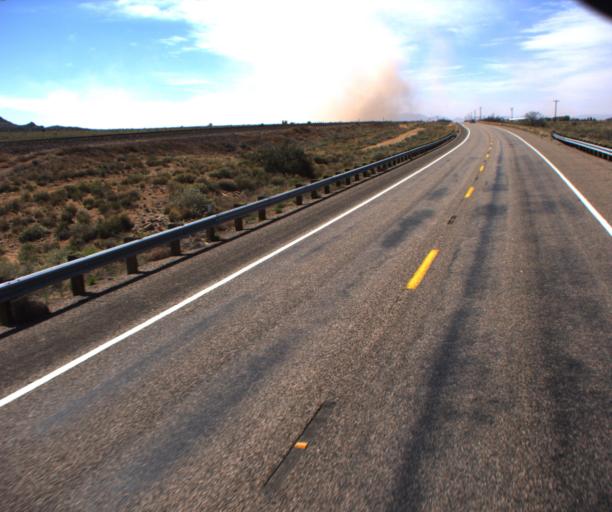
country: US
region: Arizona
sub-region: Mohave County
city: New Kingman-Butler
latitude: 35.4096
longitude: -113.7757
